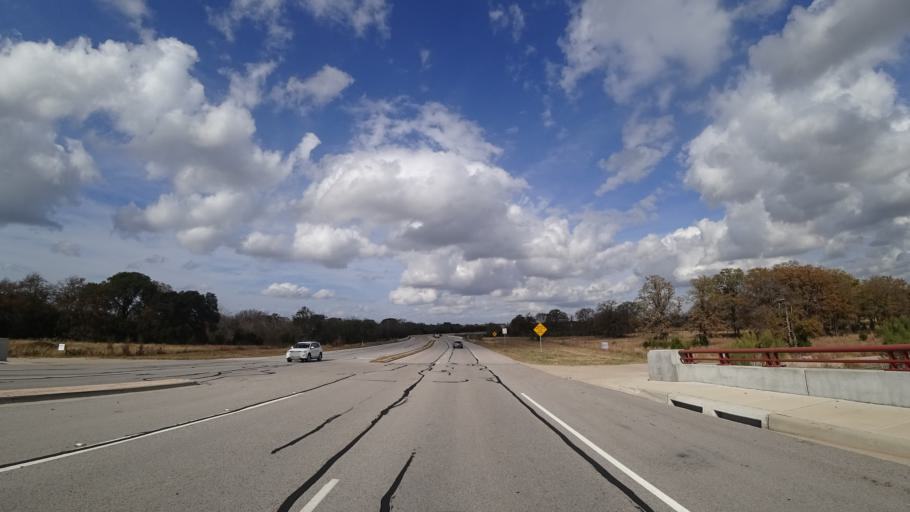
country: US
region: Texas
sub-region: Williamson County
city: Brushy Creek
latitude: 30.4819
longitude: -97.7195
